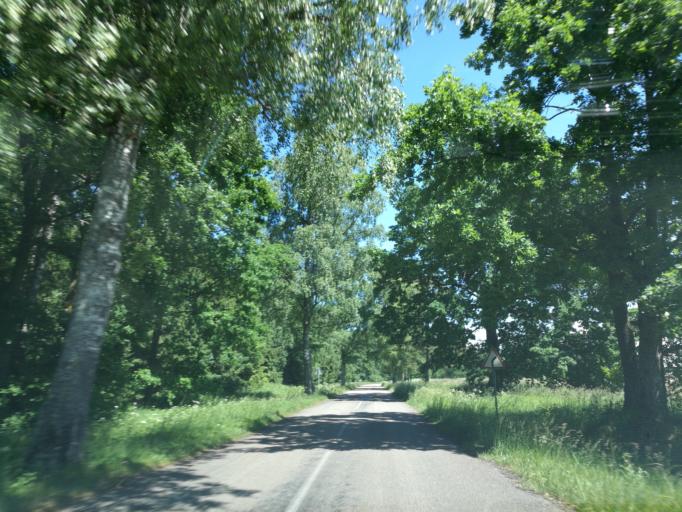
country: LT
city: Neringa
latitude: 55.3824
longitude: 21.2304
